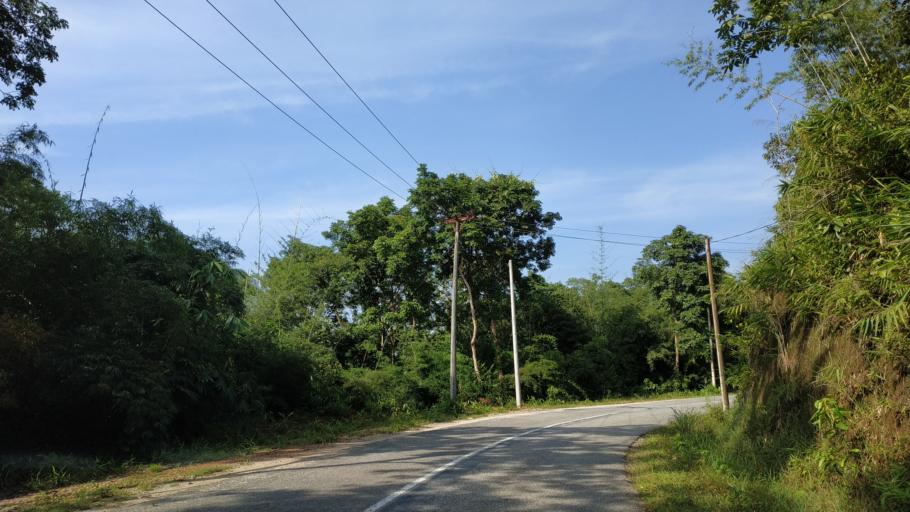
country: TH
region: Kanchanaburi
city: Thong Pha Phum
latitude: 14.6261
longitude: 98.1191
